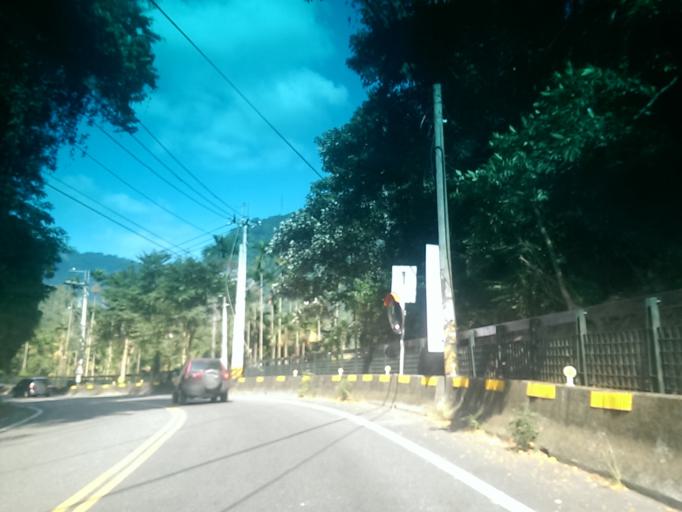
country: TW
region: Taiwan
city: Lugu
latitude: 23.8274
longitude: 120.8621
